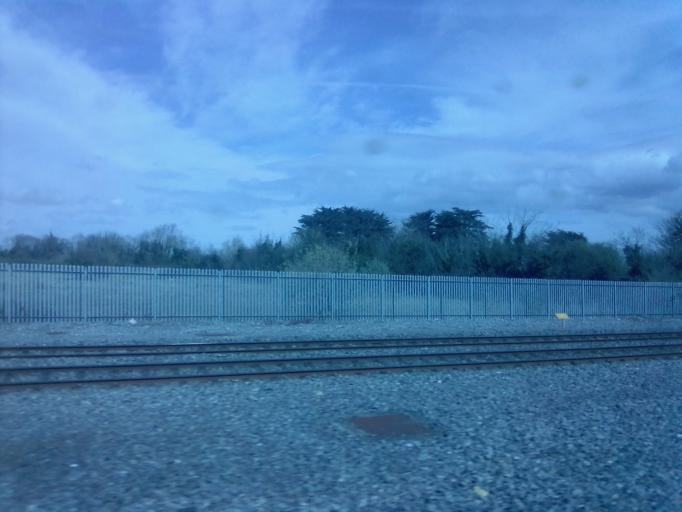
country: IE
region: Leinster
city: Clondalkin
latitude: 53.3333
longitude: -6.4034
